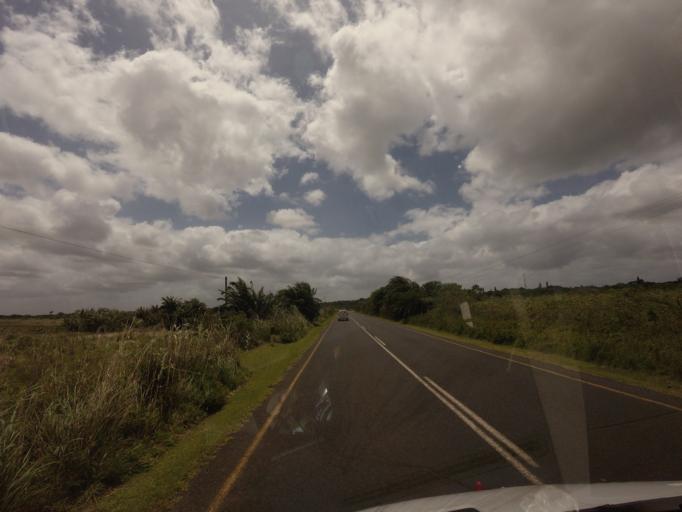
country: ZA
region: KwaZulu-Natal
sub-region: uMkhanyakude District Municipality
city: Mtubatuba
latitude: -28.3709
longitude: 32.4046
